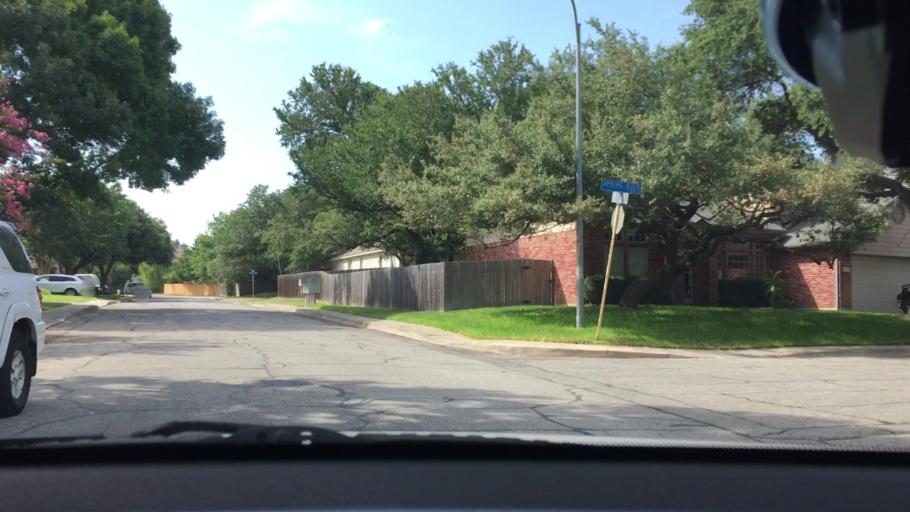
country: US
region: Texas
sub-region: Bexar County
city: Live Oak
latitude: 29.5811
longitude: -98.3801
